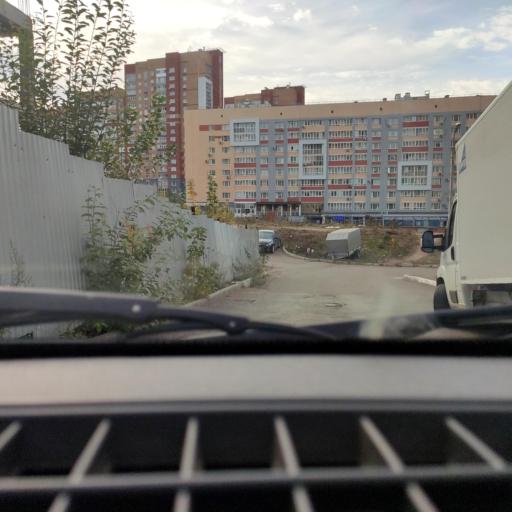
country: RU
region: Bashkortostan
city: Ufa
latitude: 54.7165
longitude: 55.9804
